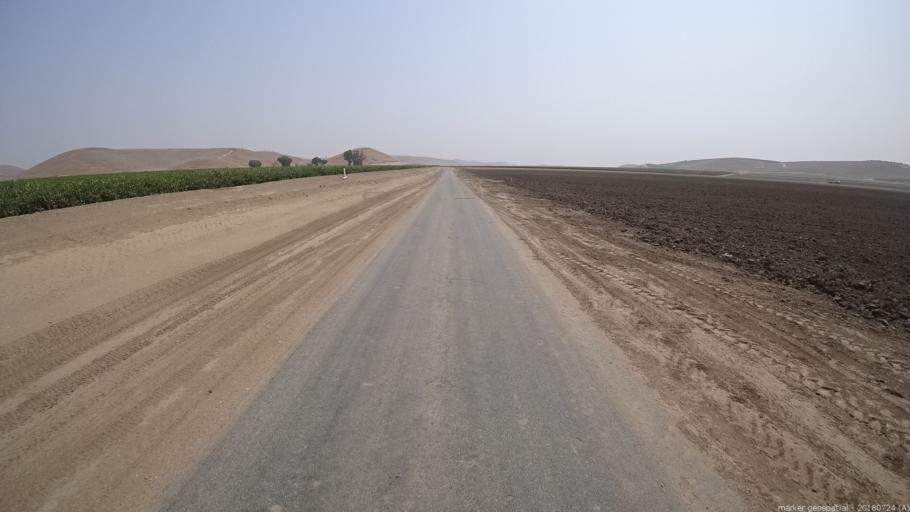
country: US
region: California
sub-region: Monterey County
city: King City
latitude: 36.1571
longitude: -121.0200
